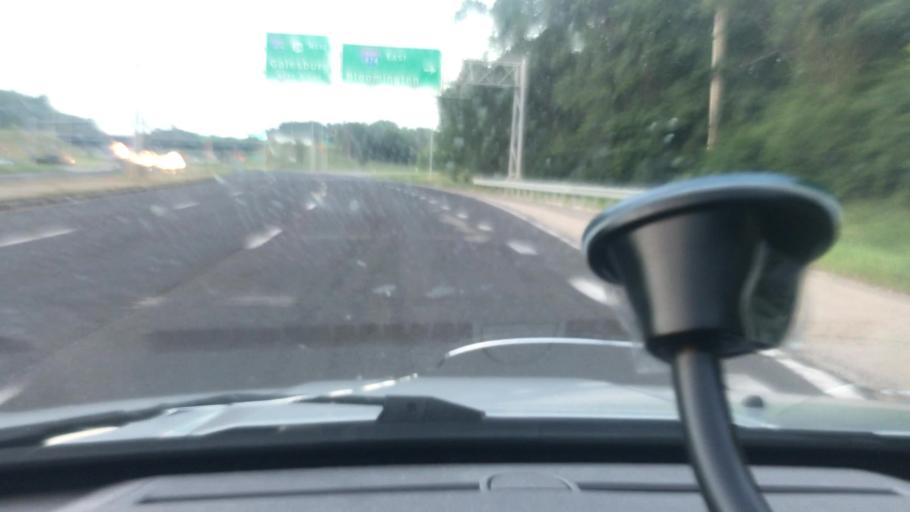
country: US
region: Illinois
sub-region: Tazewell County
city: North Pekin
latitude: 40.6275
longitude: -89.6152
